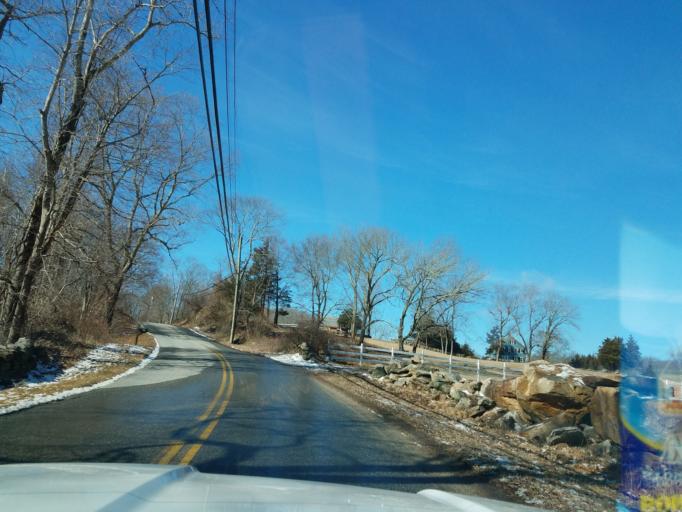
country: US
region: Connecticut
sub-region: New London County
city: Old Mystic
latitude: 41.4496
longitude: -71.9130
